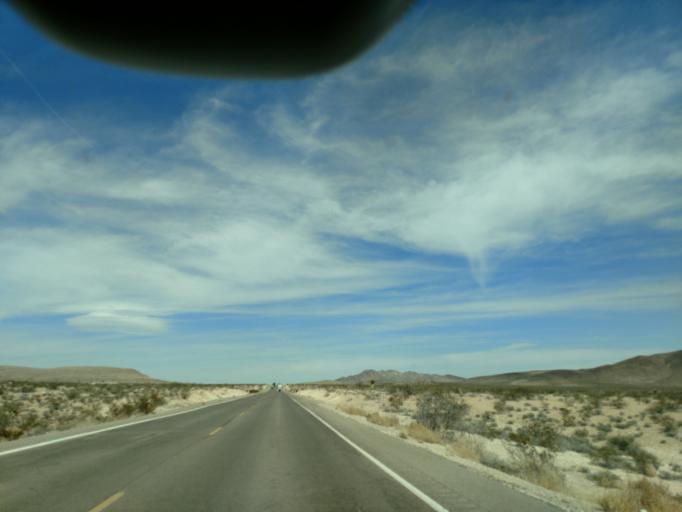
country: US
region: Nevada
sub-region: Clark County
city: Enterprise
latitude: 35.8480
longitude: -115.2633
